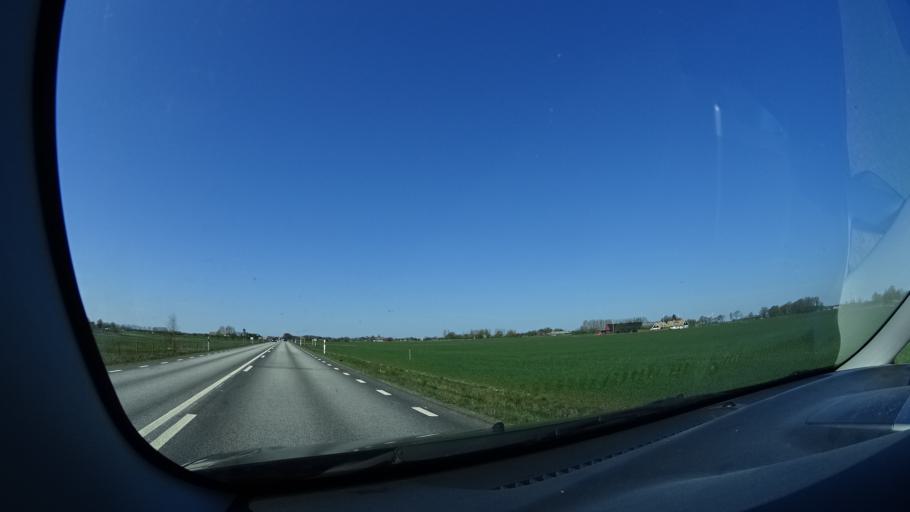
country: SE
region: Skane
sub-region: Hoganas Kommun
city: Hoganas
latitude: 56.2078
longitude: 12.6304
